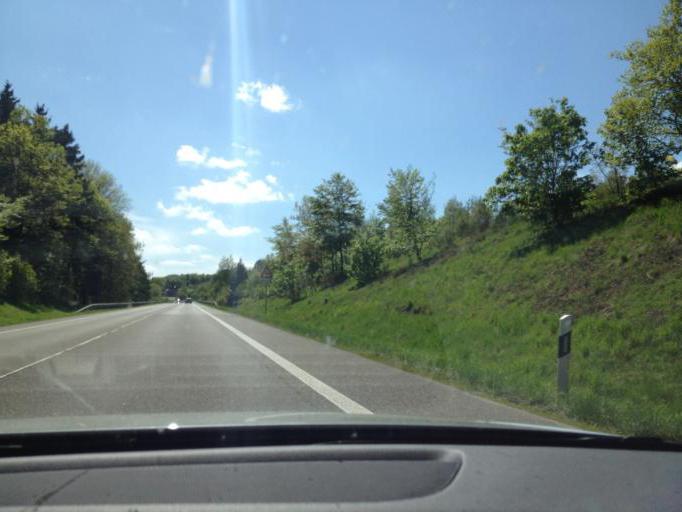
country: DE
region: Rheinland-Pfalz
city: Reuth
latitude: 50.3109
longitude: 6.4944
